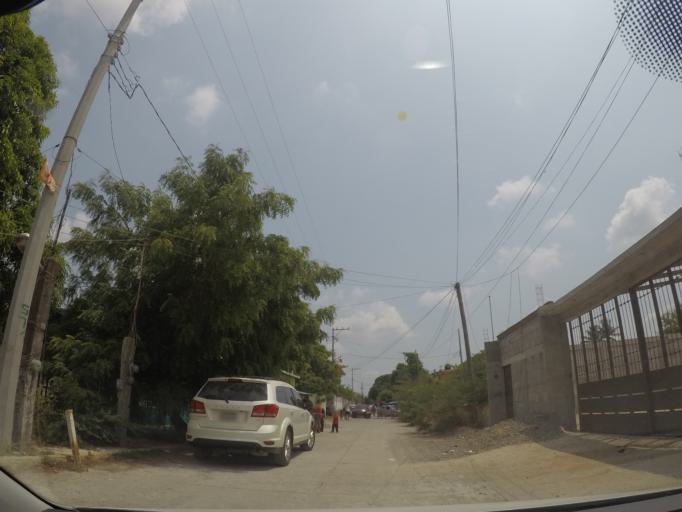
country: MX
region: Oaxaca
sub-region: El Espinal
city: El Espinal
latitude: 16.4768
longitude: -95.0434
